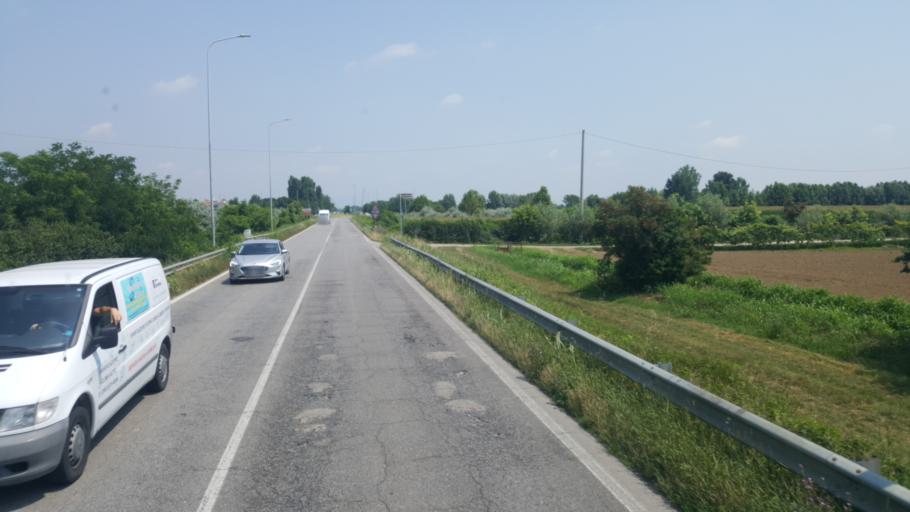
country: IT
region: Lombardy
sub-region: Provincia di Brescia
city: Manerbio
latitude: 45.3388
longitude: 10.1452
